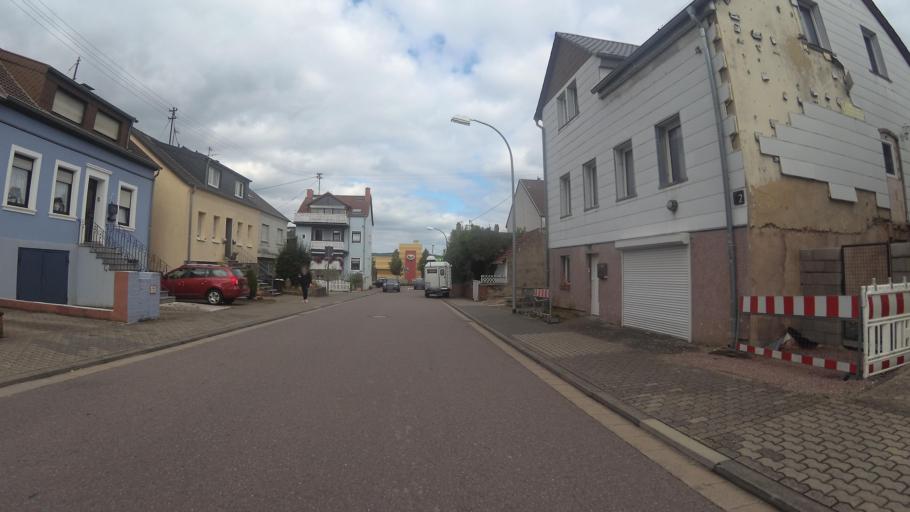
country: FR
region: Lorraine
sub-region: Departement de la Moselle
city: Schoeneck
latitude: 49.2389
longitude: 6.9154
